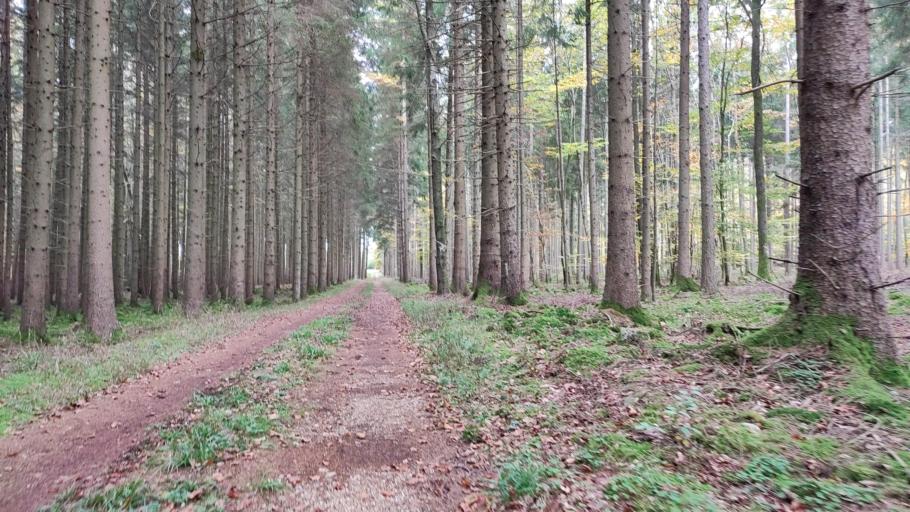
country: DE
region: Bavaria
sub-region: Swabia
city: Munsterhausen
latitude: 48.3237
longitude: 10.4967
